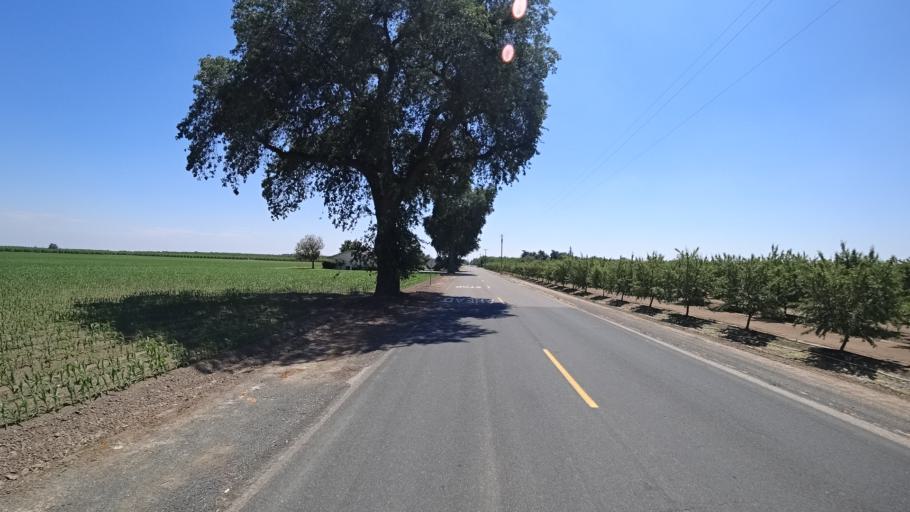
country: US
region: California
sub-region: Kings County
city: Lucerne
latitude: 36.4147
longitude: -119.6548
